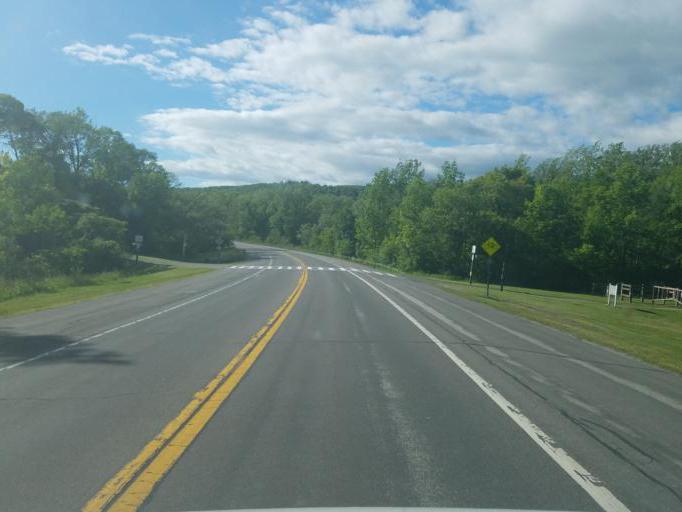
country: US
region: New York
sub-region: Herkimer County
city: Little Falls
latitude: 43.0284
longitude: -74.8210
